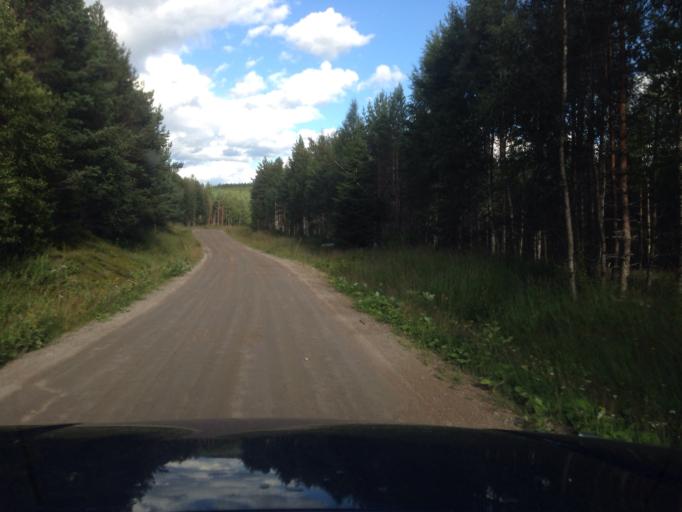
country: SE
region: Dalarna
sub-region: Ludvika Kommun
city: Abborrberget
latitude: 60.3047
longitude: 14.6295
